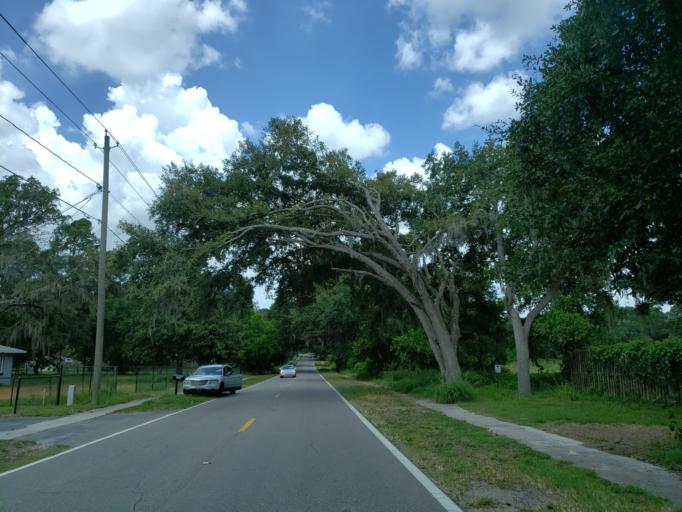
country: US
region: Florida
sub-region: Hillsborough County
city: Seffner
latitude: 27.9961
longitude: -82.2918
